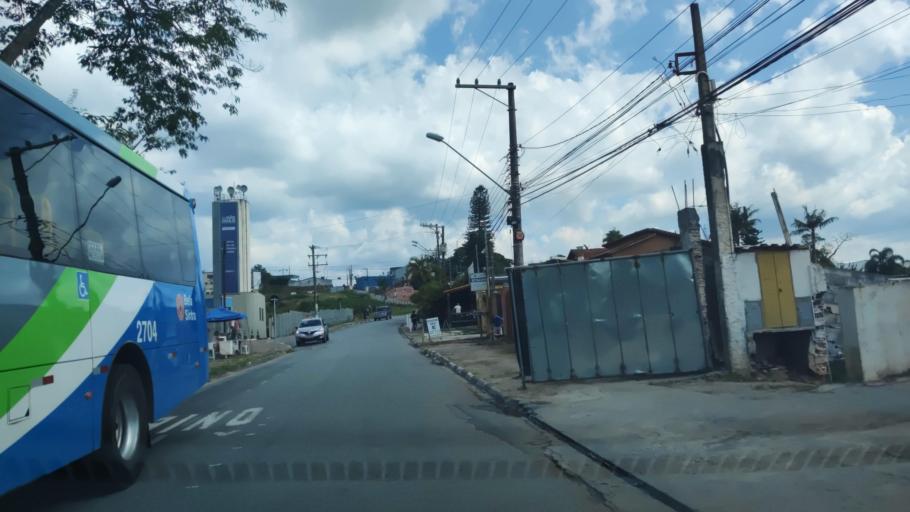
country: BR
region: Sao Paulo
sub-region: Itapecerica Da Serra
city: Itapecerica da Serra
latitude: -23.7003
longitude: -46.8484
